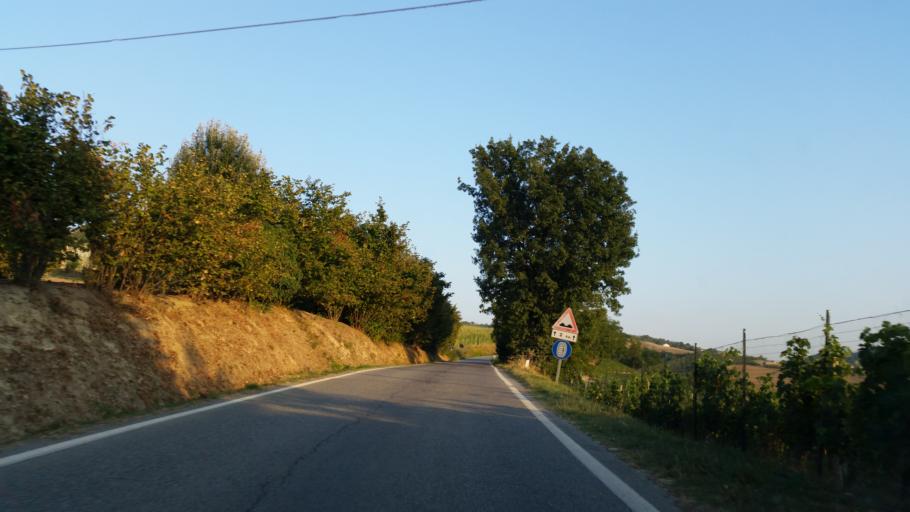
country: IT
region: Piedmont
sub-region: Provincia di Cuneo
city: Trezzo Tinella
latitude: 44.6576
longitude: 8.0989
